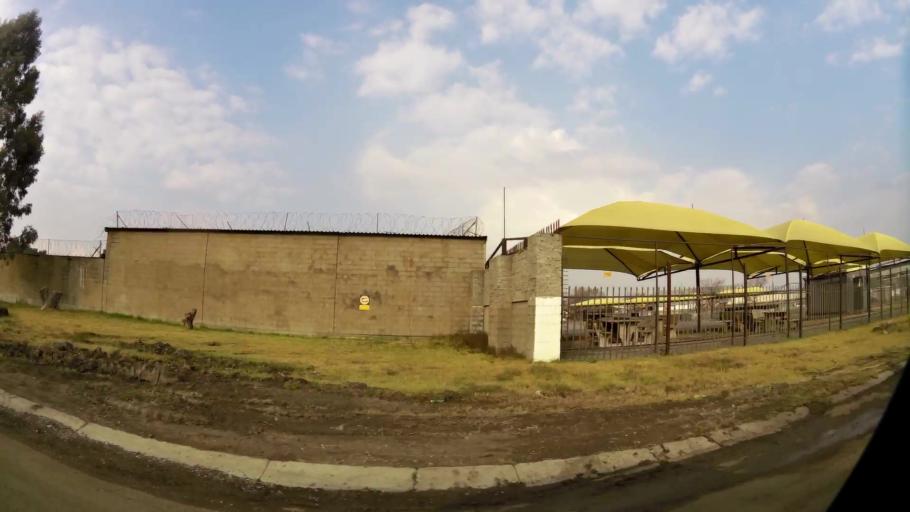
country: ZA
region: Gauteng
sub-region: Sedibeng District Municipality
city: Vereeniging
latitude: -26.6830
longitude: 27.9111
